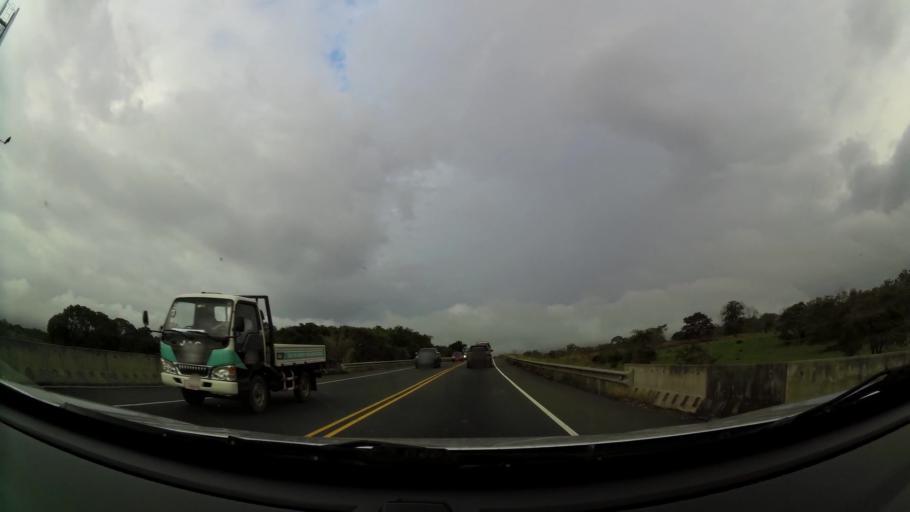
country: CR
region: Alajuela
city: Carrillos
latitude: 9.9659
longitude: -84.2993
